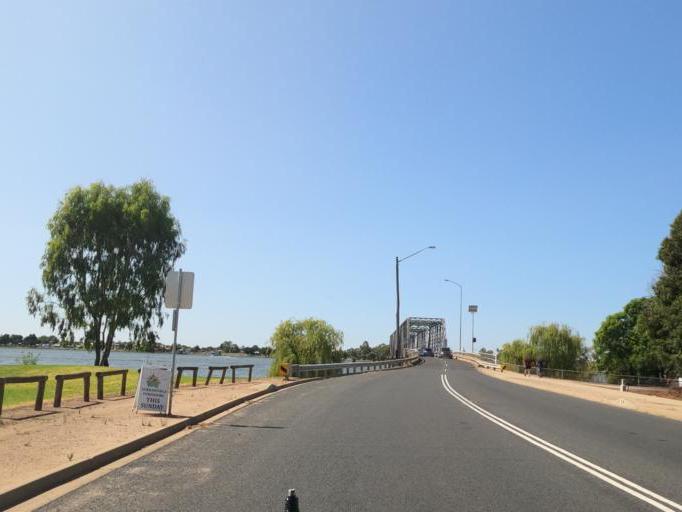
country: AU
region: New South Wales
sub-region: Corowa Shire
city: Mulwala
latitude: -36.0029
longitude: 146.0032
